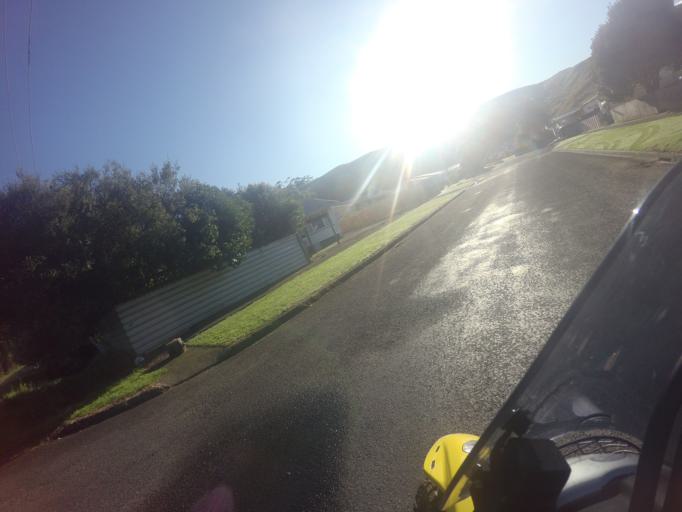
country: NZ
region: Gisborne
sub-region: Gisborne District
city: Gisborne
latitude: -38.6706
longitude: 178.0582
